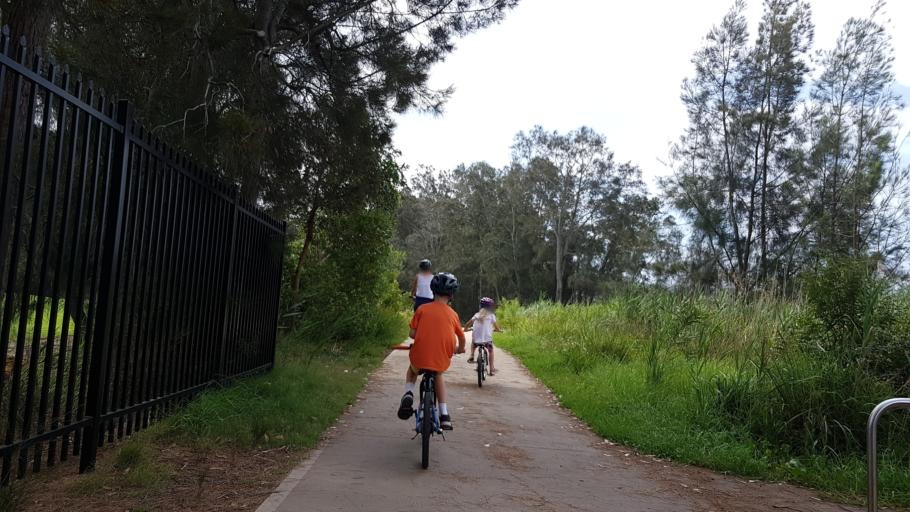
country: AU
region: New South Wales
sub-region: Warringah
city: Narrabeen
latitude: -33.7223
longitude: 151.2725
